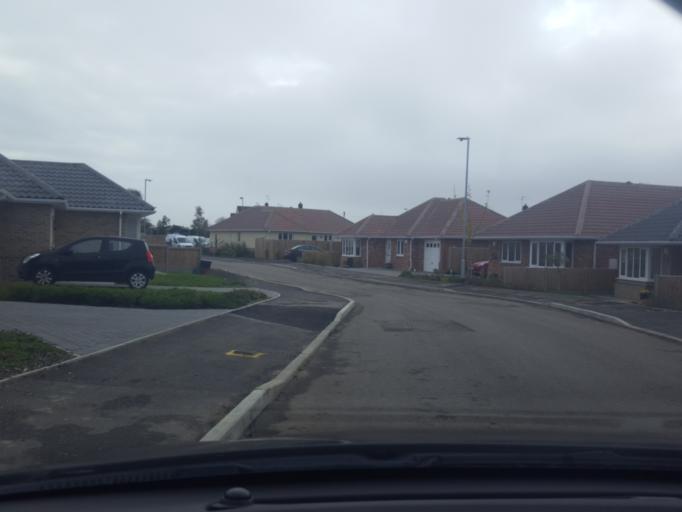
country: GB
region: England
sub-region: Essex
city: Clacton-on-Sea
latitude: 51.8004
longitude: 1.1742
